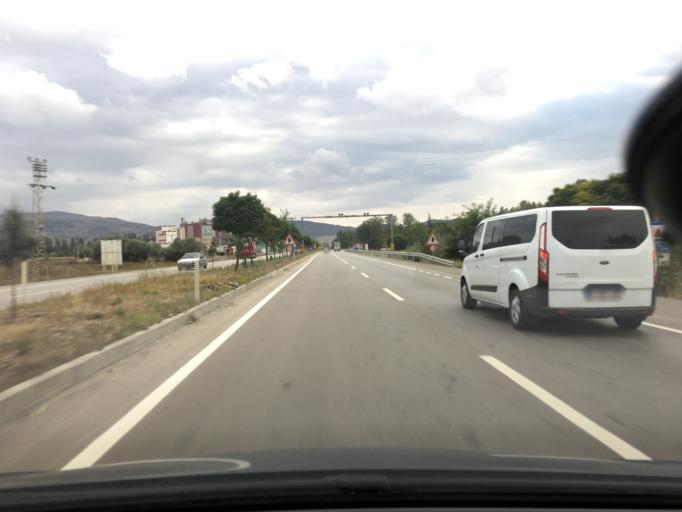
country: TR
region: Afyonkarahisar
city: Sincanli
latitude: 38.7488
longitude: 30.3568
